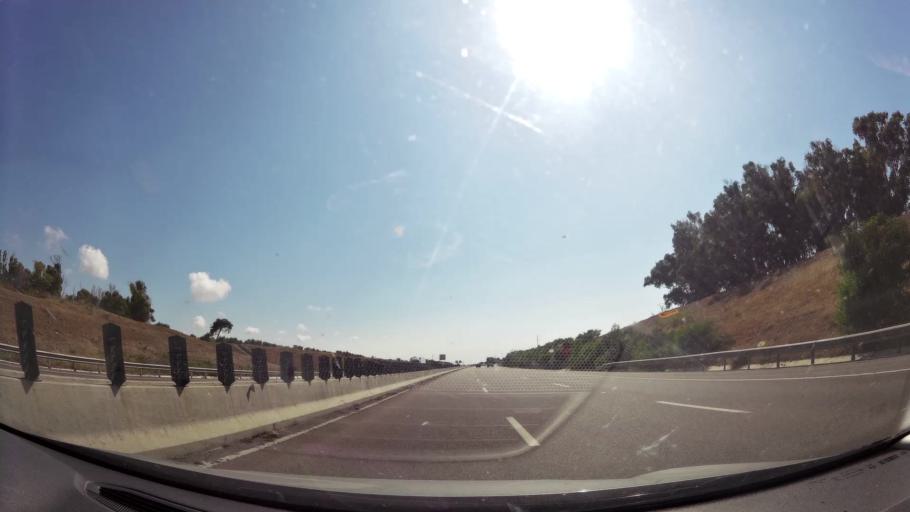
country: MA
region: Chaouia-Ouardigha
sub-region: Benslimane
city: Bouznika
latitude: 33.8200
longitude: -7.1195
